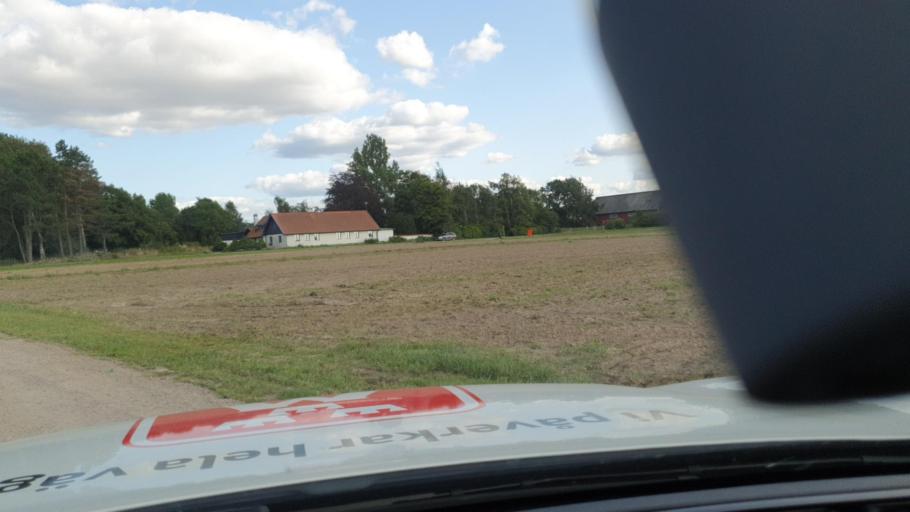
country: SE
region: Skane
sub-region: Angelholms Kommun
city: AEngelholm
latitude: 56.1976
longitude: 12.8508
